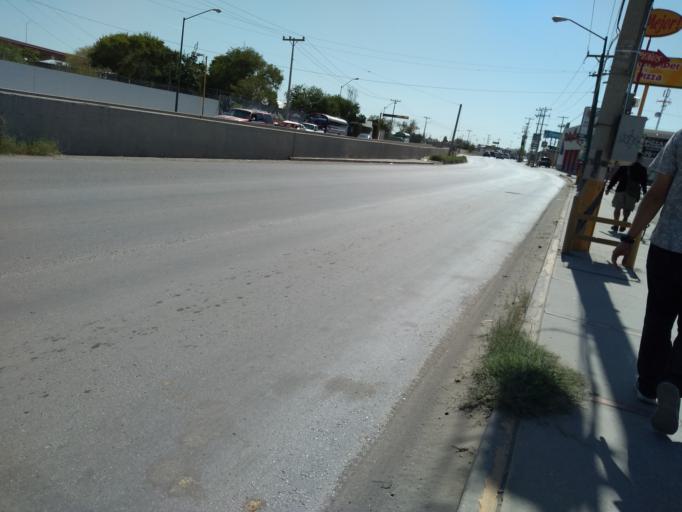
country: US
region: Texas
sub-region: El Paso County
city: El Paso
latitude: 31.7535
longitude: -106.4993
